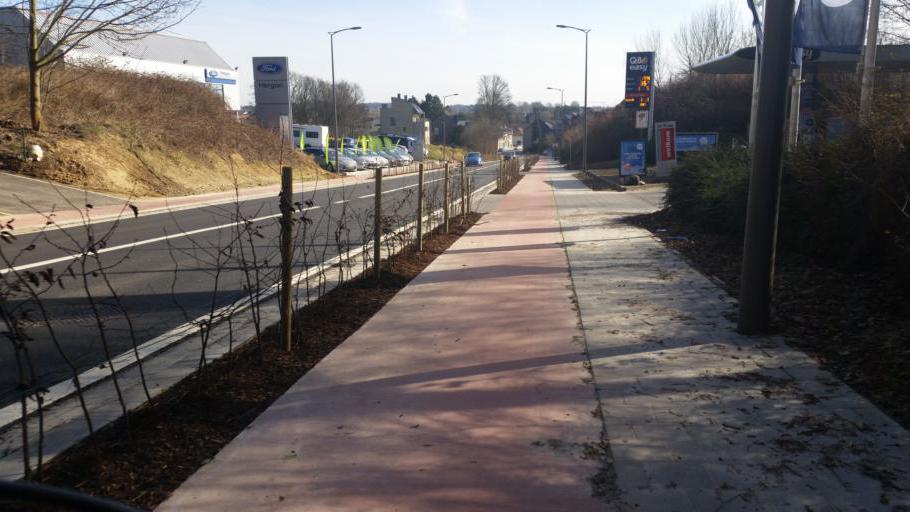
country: BE
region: Flanders
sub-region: Provincie Vlaams-Brabant
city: Wezembeek-Oppem
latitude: 50.8659
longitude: 4.5135
